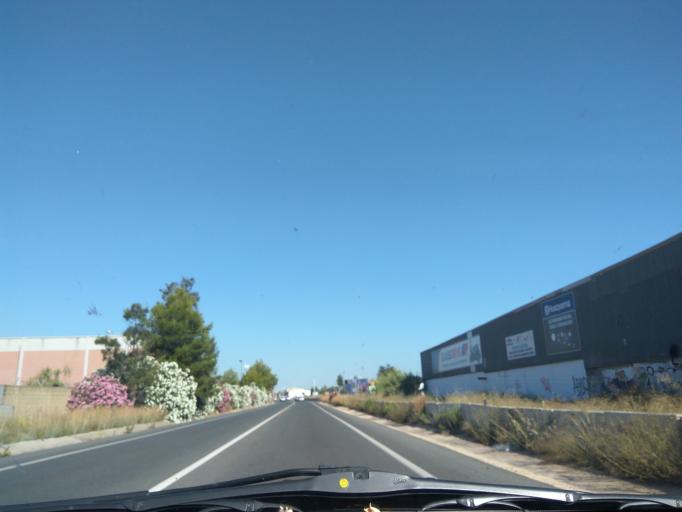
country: ES
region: Valencia
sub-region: Provincia de Valencia
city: Manises
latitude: 39.4945
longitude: -0.4724
